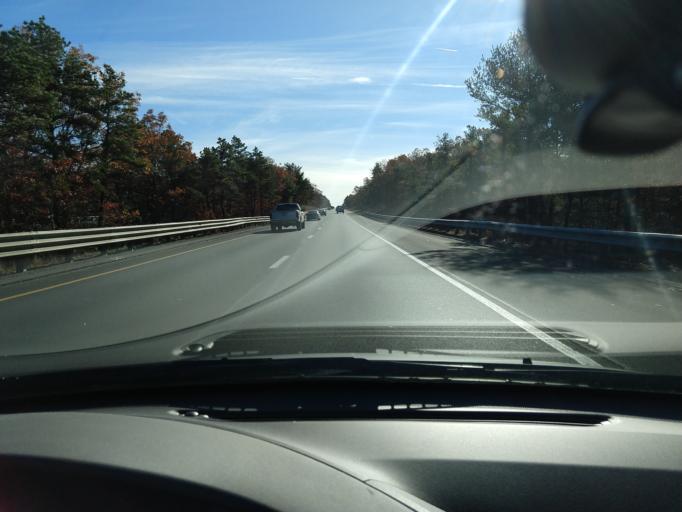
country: US
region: Massachusetts
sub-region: Plymouth County
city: Plymouth
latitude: 41.9025
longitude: -70.6168
